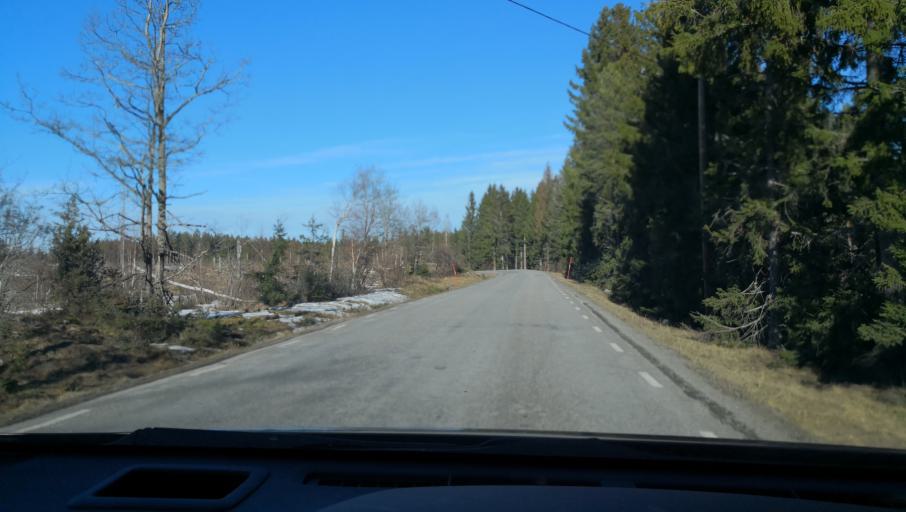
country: SE
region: Uppsala
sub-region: Osthammars Kommun
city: Osterbybruk
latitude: 60.2275
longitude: 17.9191
